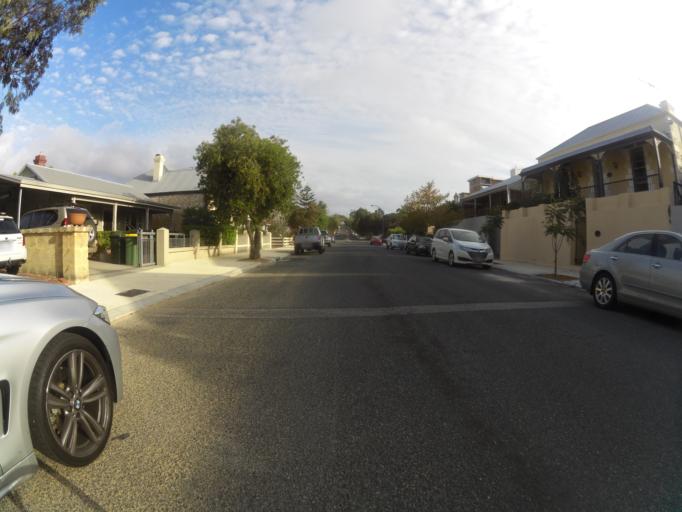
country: AU
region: Western Australia
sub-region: East Fremantle
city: East Fremantle
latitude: -32.0432
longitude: 115.7591
